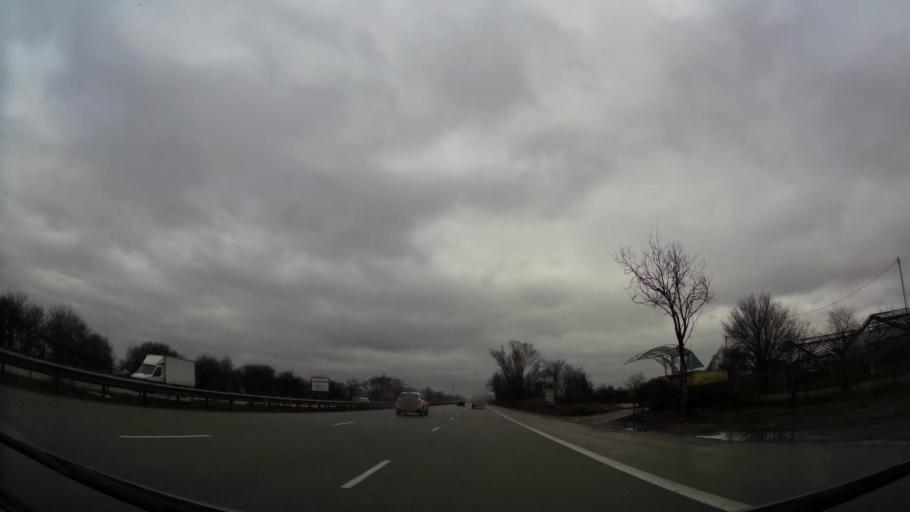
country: BG
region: Sofia-Capital
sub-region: Stolichna Obshtina
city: Sofia
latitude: 42.6393
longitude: 23.4501
